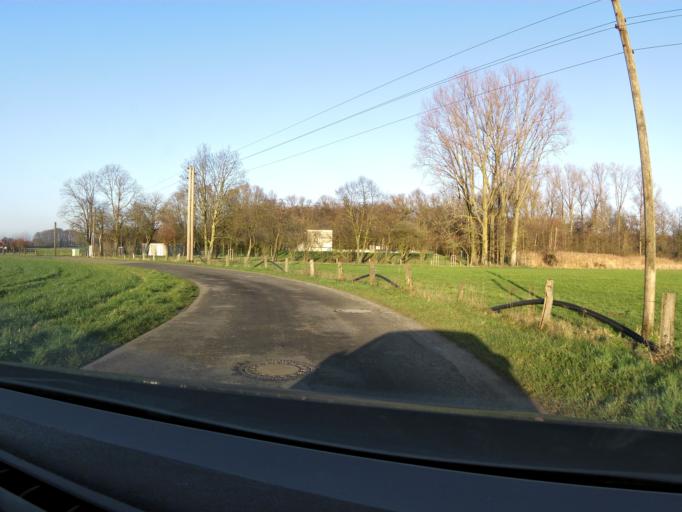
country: DE
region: North Rhine-Westphalia
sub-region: Regierungsbezirk Dusseldorf
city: Nettetal
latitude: 51.3310
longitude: 6.2372
